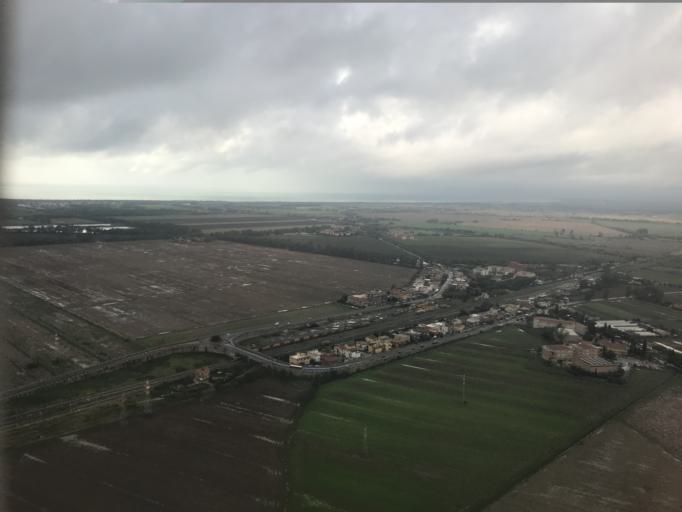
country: IT
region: Latium
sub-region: Citta metropolitana di Roma Capitale
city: Maccarese
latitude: 41.8739
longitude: 12.2502
